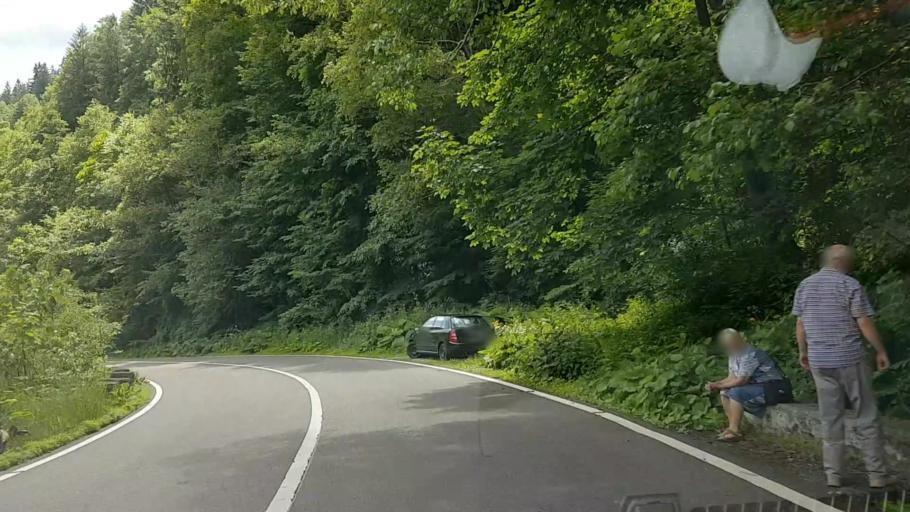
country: RO
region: Suceava
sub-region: Comuna Crucea
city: Crucea
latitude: 47.3149
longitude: 25.6251
